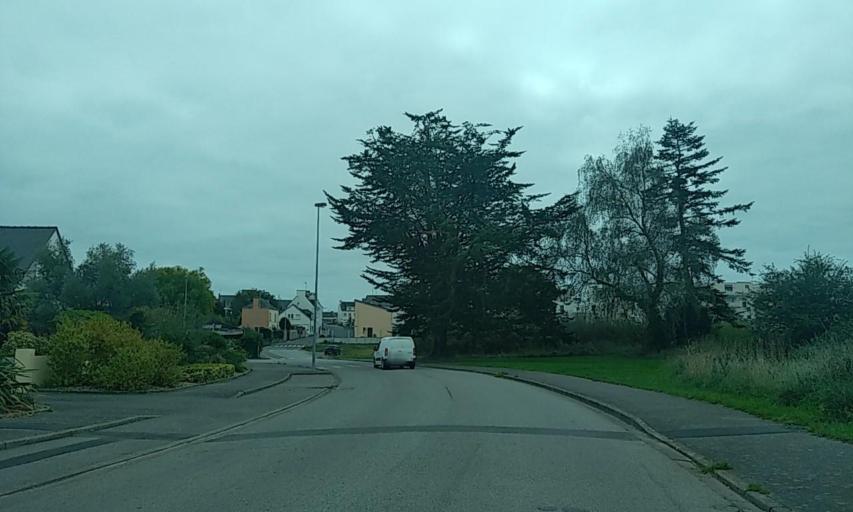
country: FR
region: Brittany
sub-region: Departement du Morbihan
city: Lorient
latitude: 47.7682
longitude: -3.3612
